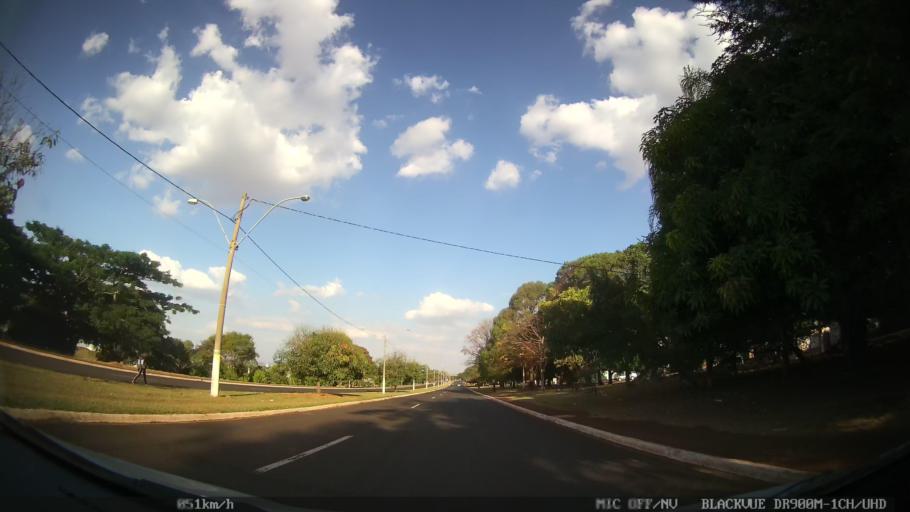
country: BR
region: Sao Paulo
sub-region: Ribeirao Preto
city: Ribeirao Preto
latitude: -21.1330
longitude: -47.8395
